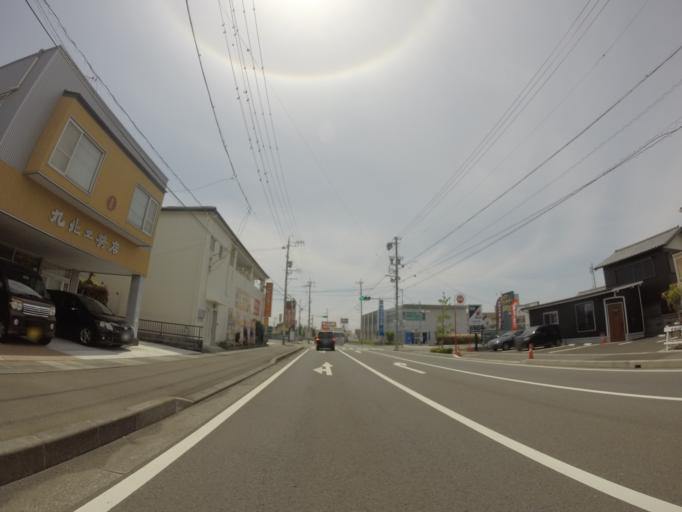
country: JP
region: Shizuoka
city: Yaizu
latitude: 34.8402
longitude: 138.3082
